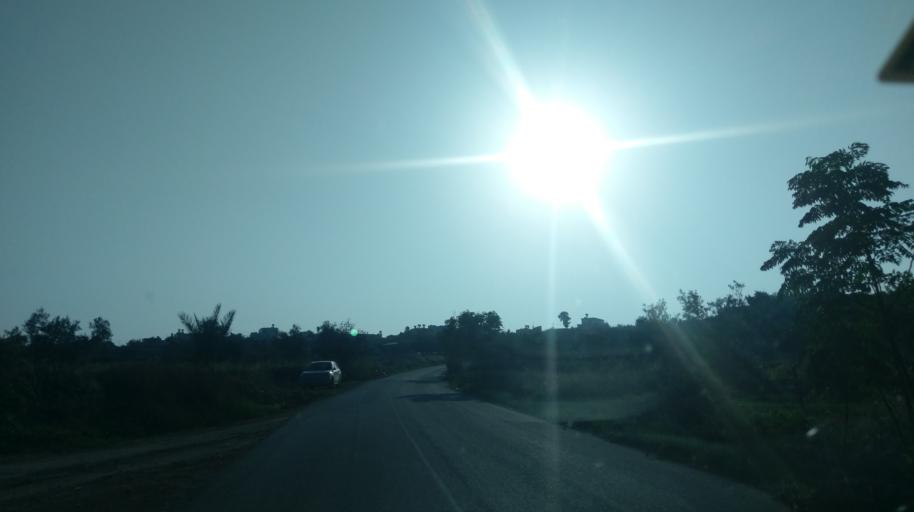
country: CY
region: Ammochostos
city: Leonarisso
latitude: 35.4267
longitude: 34.0765
